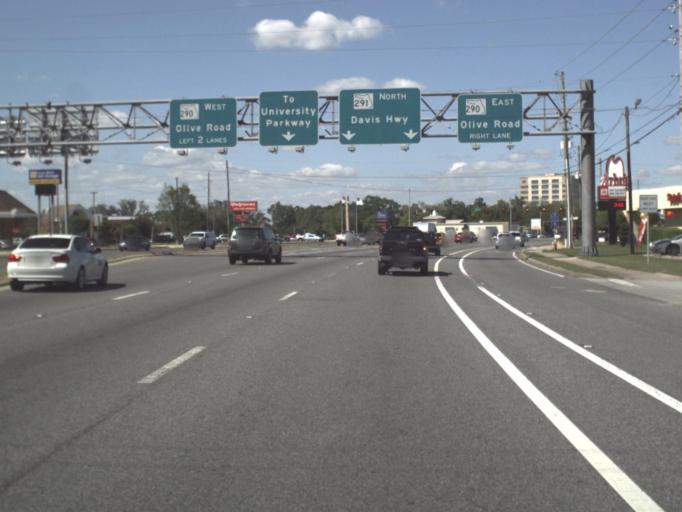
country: US
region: Florida
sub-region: Escambia County
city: Ferry Pass
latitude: 30.5085
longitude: -87.2212
